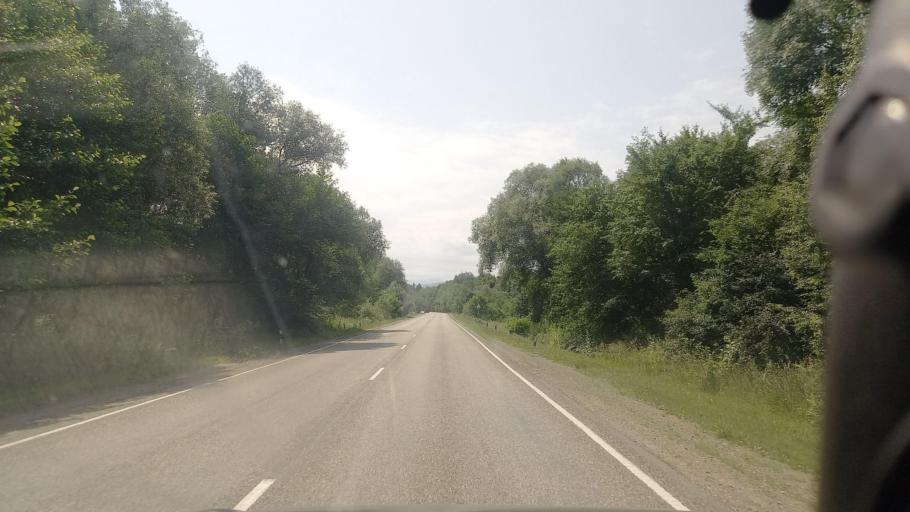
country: RU
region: Krasnodarskiy
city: Psebay
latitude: 44.0671
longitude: 40.8622
